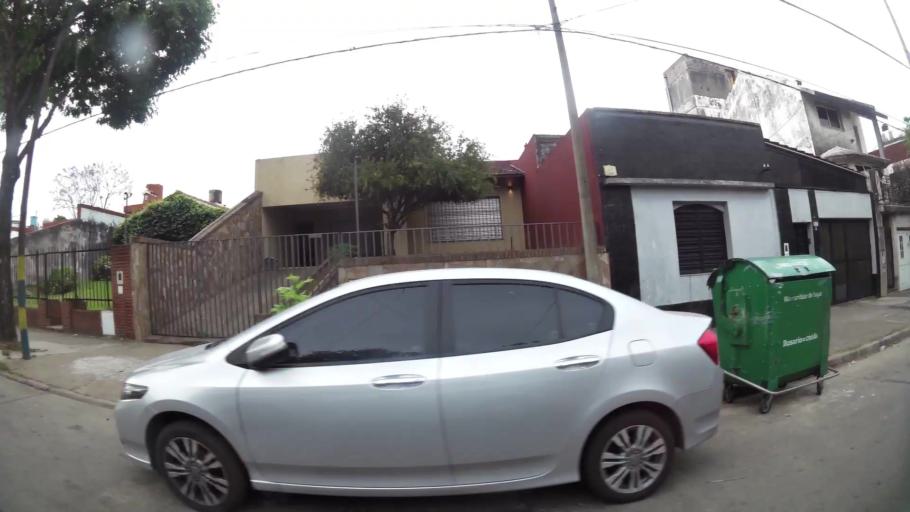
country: AR
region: Santa Fe
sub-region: Departamento de Rosario
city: Rosario
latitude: -32.9153
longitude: -60.6886
